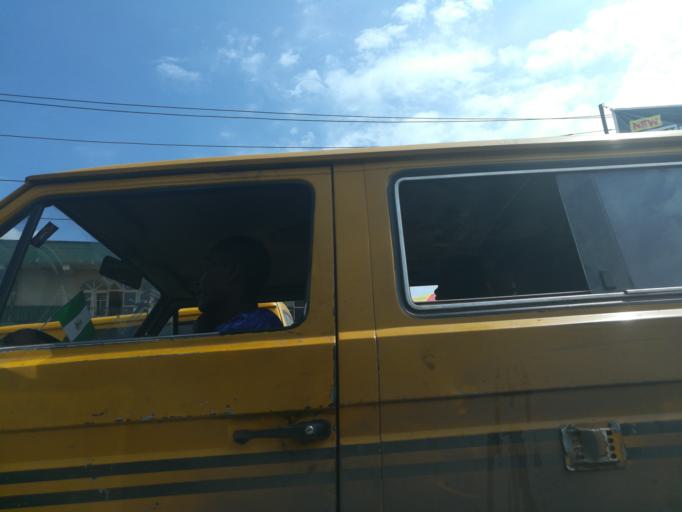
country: NG
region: Lagos
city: Agege
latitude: 6.6225
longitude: 3.3257
